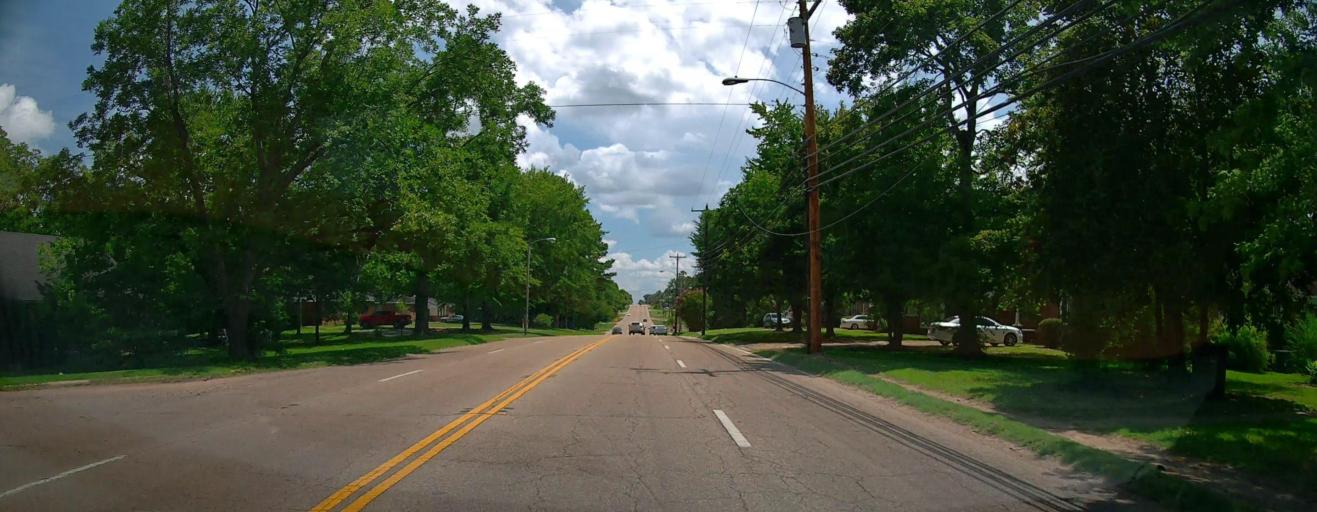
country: US
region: Mississippi
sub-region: Lee County
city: Verona
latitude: 34.1902
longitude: -88.7199
